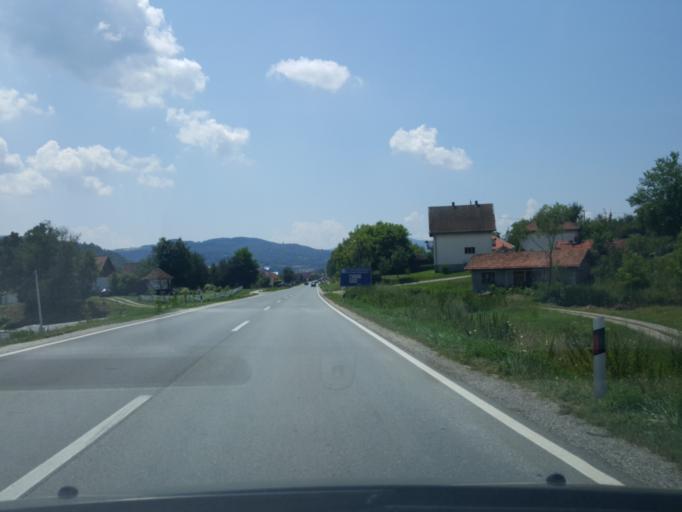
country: RS
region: Central Serbia
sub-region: Moravicki Okrug
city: Gornji Milanovac
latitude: 44.0624
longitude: 20.4911
